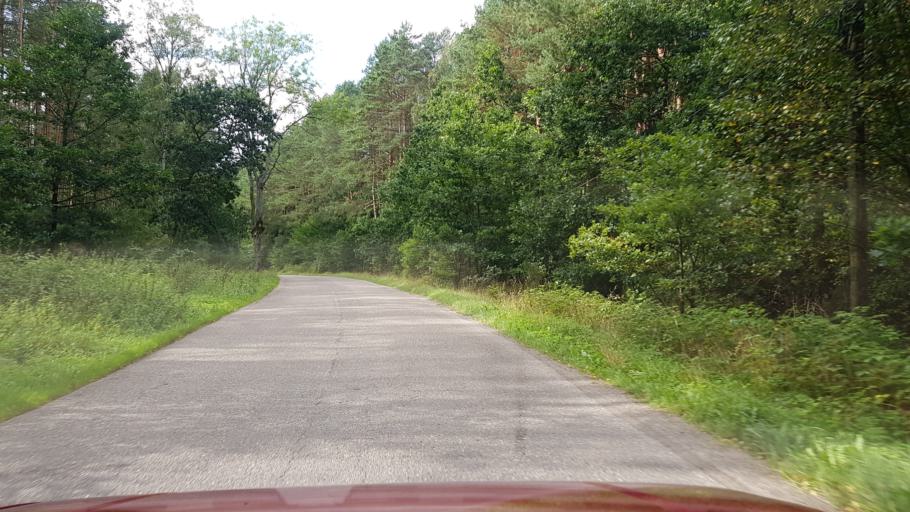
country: PL
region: West Pomeranian Voivodeship
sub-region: Powiat bialogardzki
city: Tychowo
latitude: 54.0204
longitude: 16.3922
